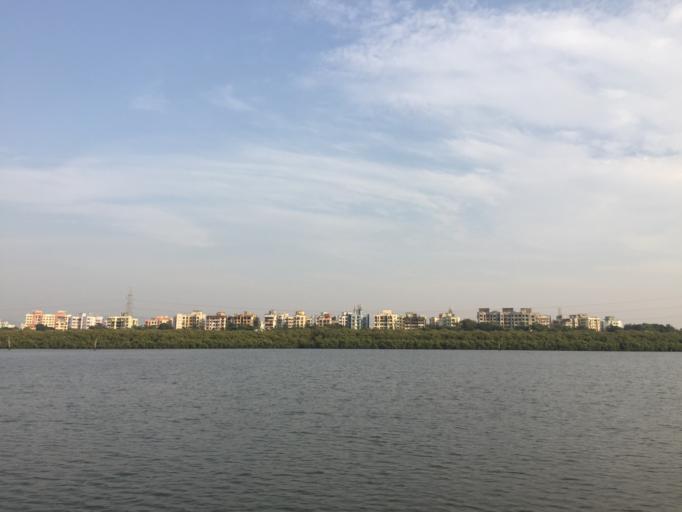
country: IN
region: Maharashtra
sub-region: Mumbai Suburban
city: Borivli
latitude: 19.2319
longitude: 72.8188
